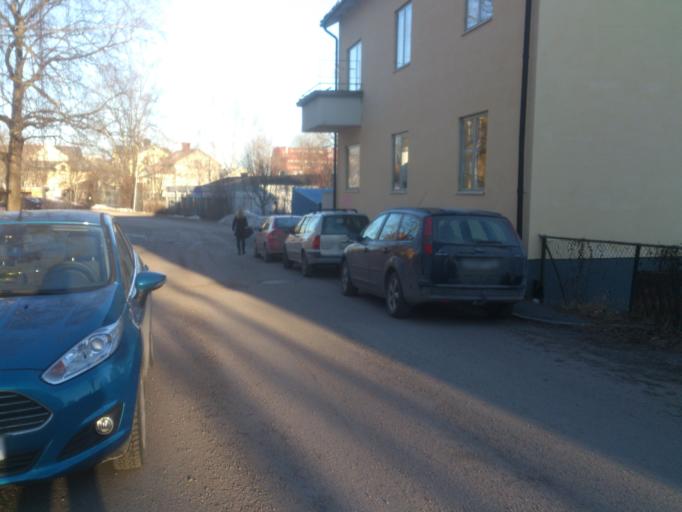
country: SE
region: Vaesternorrland
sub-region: Sundsvalls Kommun
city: Sundsvall
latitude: 62.3842
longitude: 17.3117
